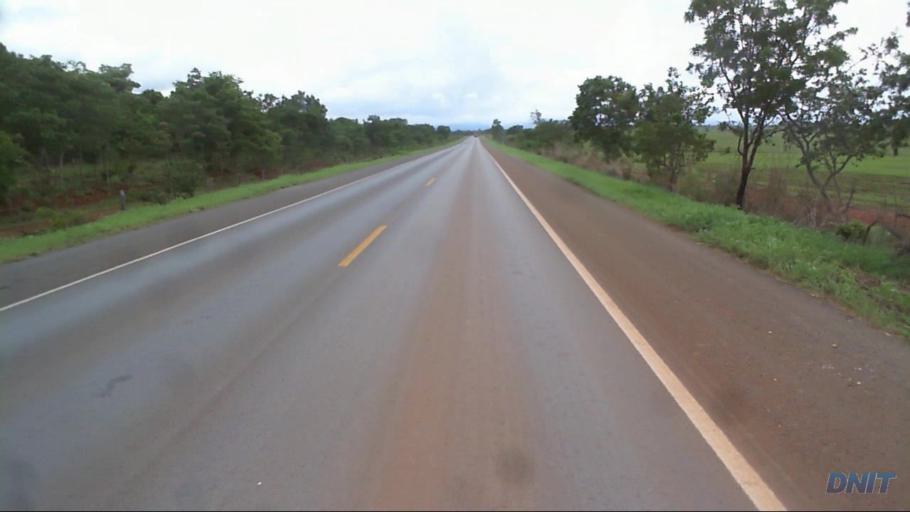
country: BR
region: Goias
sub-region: Padre Bernardo
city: Padre Bernardo
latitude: -15.1640
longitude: -48.3617
